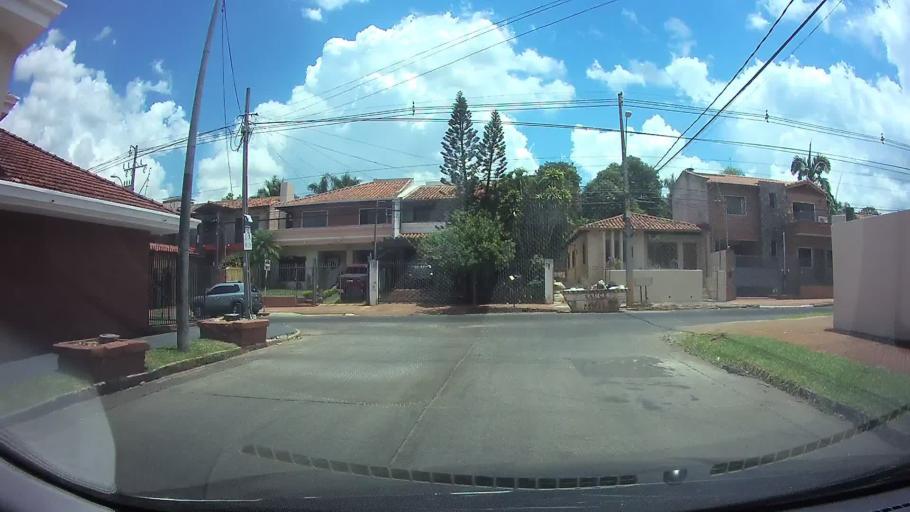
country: PY
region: Asuncion
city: Asuncion
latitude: -25.2982
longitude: -57.5977
